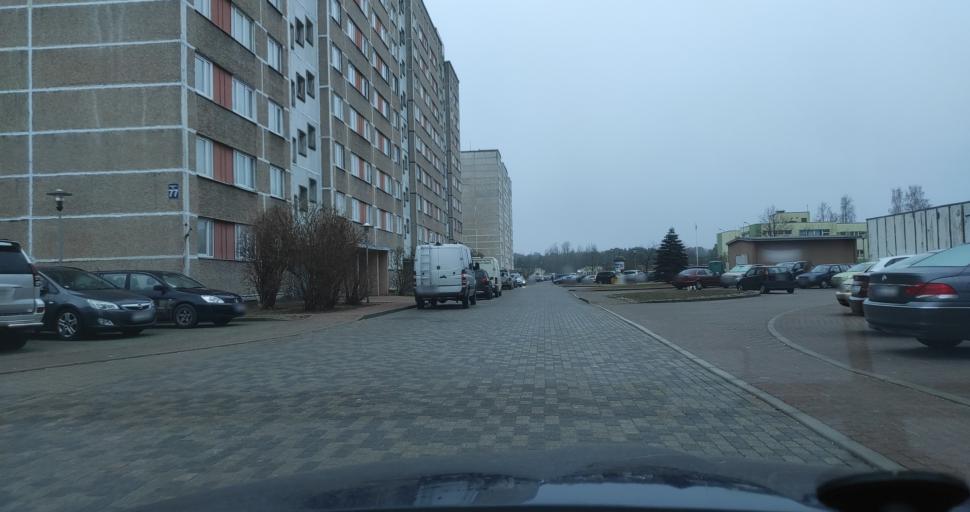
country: LV
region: Ventspils
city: Ventspils
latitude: 57.3837
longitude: 21.5499
